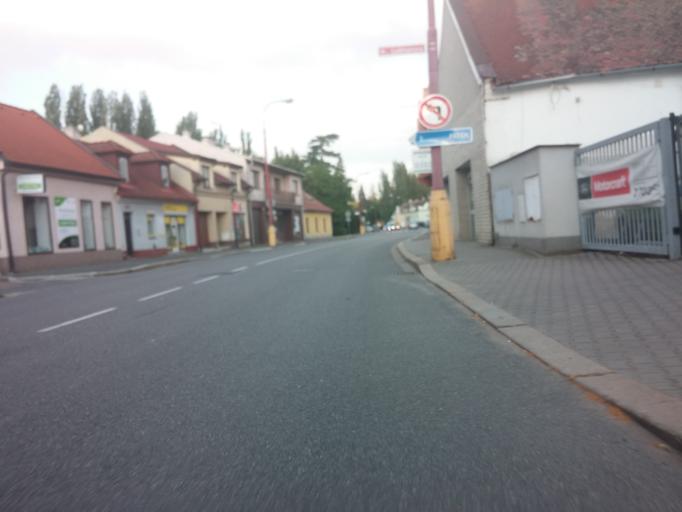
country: CZ
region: Central Bohemia
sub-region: Okres Nymburk
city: Podebrady
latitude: 50.1418
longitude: 15.1248
